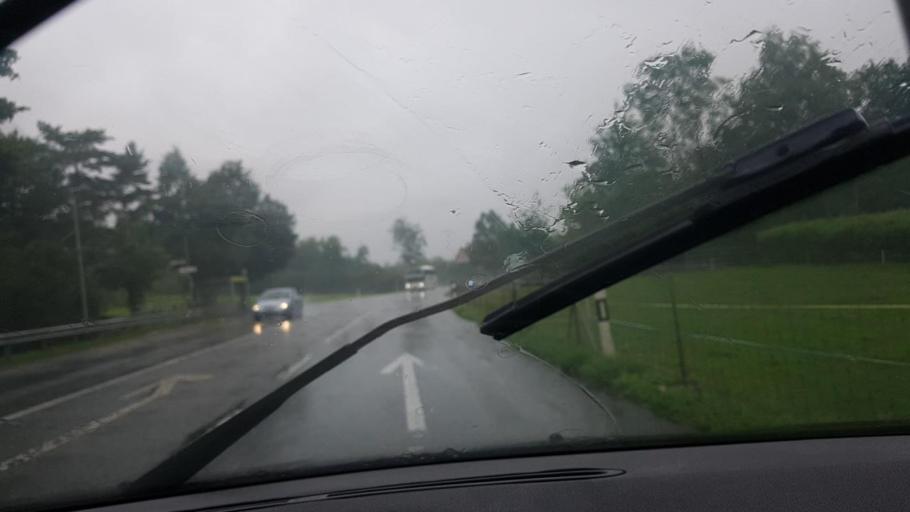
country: LI
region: Triesen
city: Triesen
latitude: 47.0935
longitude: 9.5247
